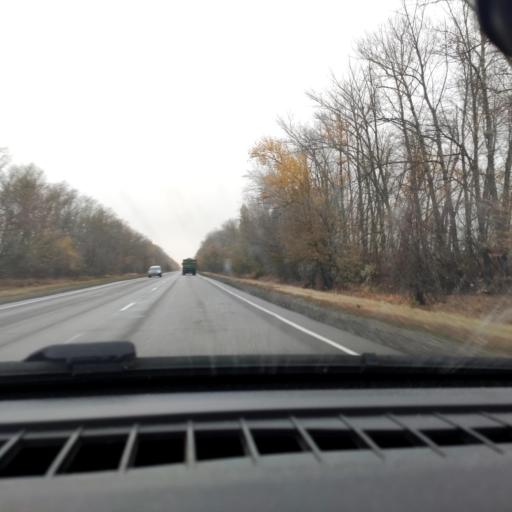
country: RU
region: Voronezj
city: Ostrogozhsk
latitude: 50.9600
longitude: 39.0261
